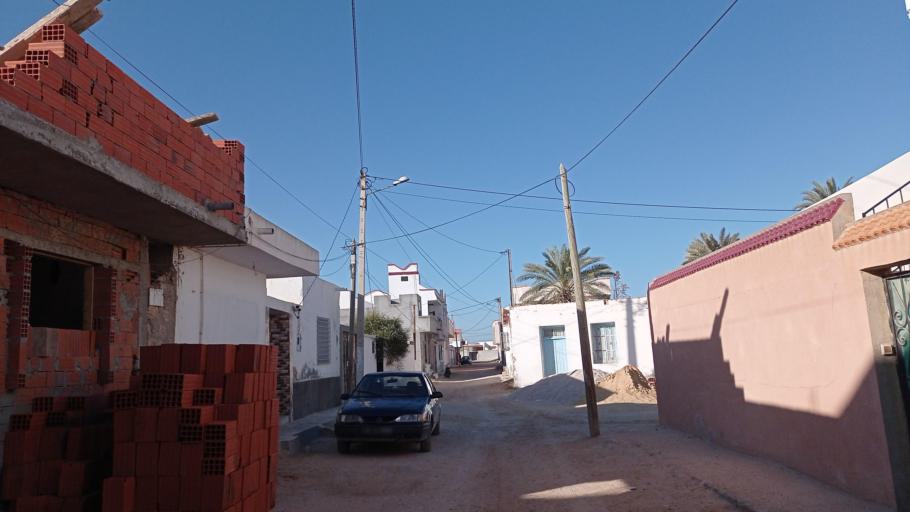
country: TN
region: Qabis
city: Gabes
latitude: 33.8451
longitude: 10.1187
